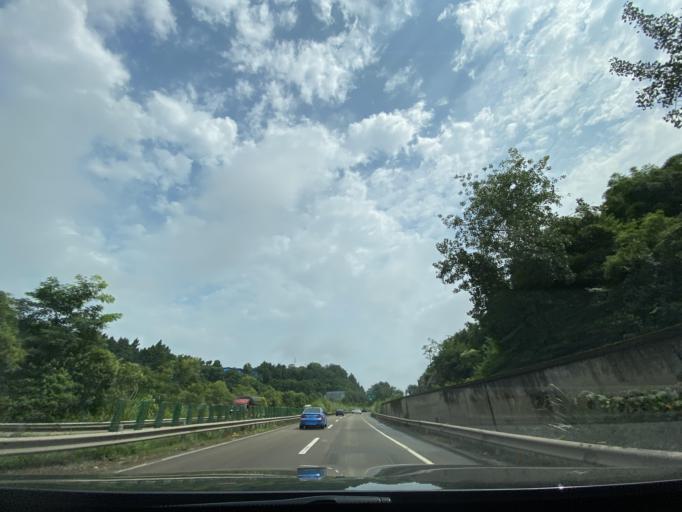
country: CN
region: Sichuan
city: Yanjiang
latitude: 29.9389
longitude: 104.6188
